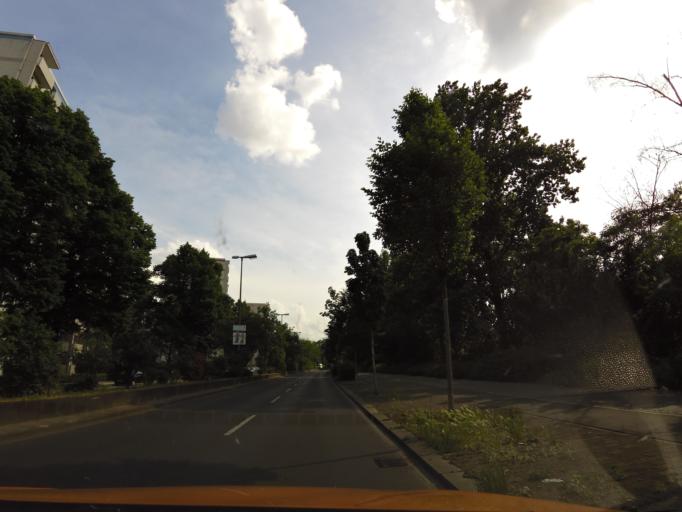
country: DE
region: Berlin
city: Hansaviertel
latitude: 52.5221
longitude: 13.3417
